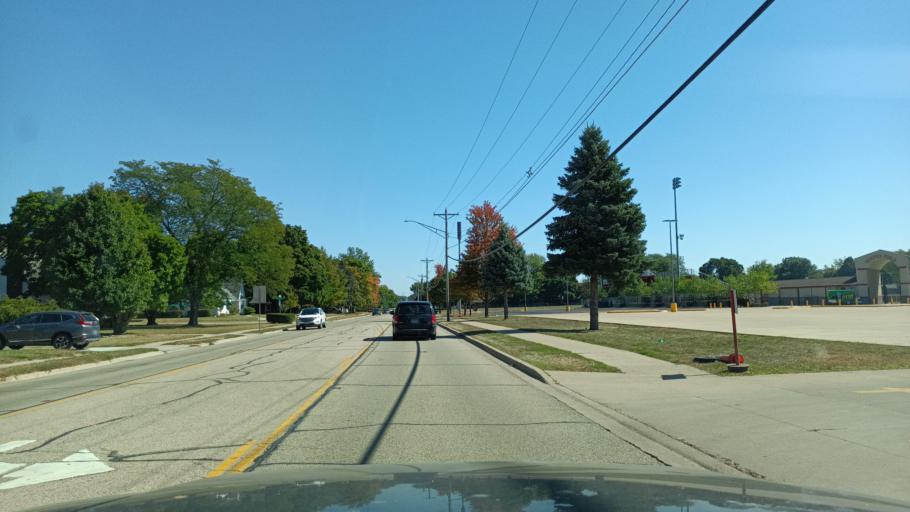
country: US
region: Illinois
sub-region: Tazewell County
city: Morton
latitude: 40.6129
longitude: -89.4535
